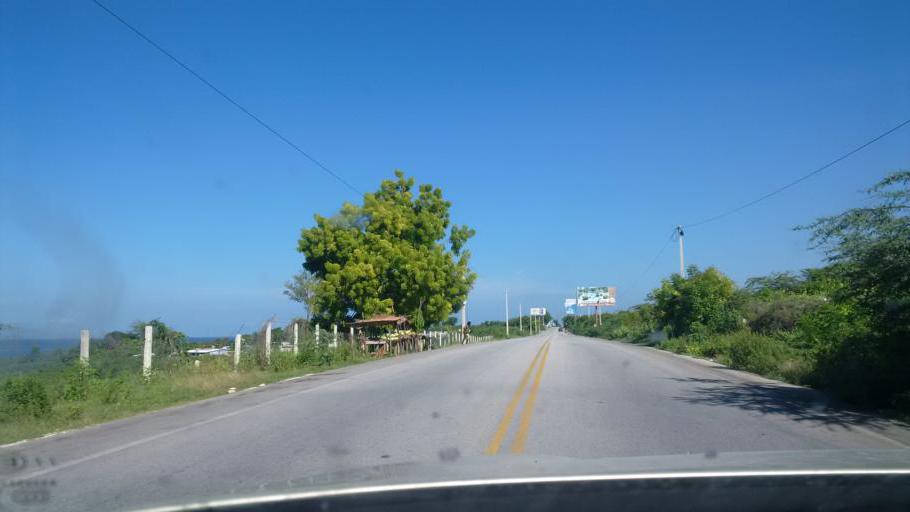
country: HT
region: Ouest
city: Cabaret
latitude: 18.8668
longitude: -72.6049
